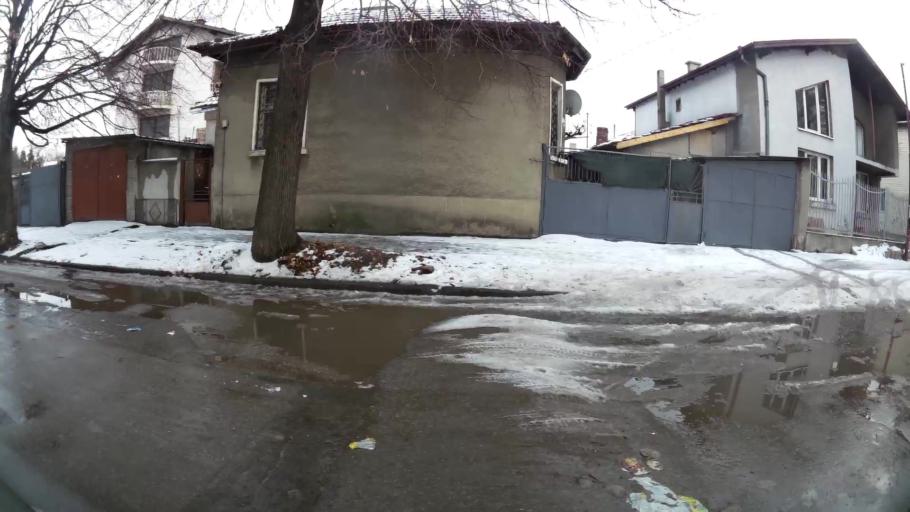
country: BG
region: Sofia-Capital
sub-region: Stolichna Obshtina
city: Sofia
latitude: 42.6876
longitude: 23.3823
